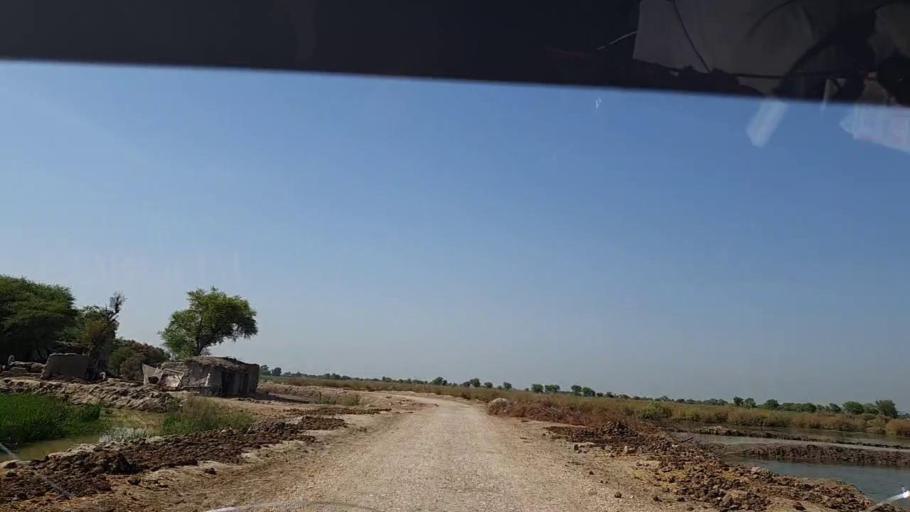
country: PK
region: Sindh
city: Tangwani
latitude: 28.3273
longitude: 69.0793
